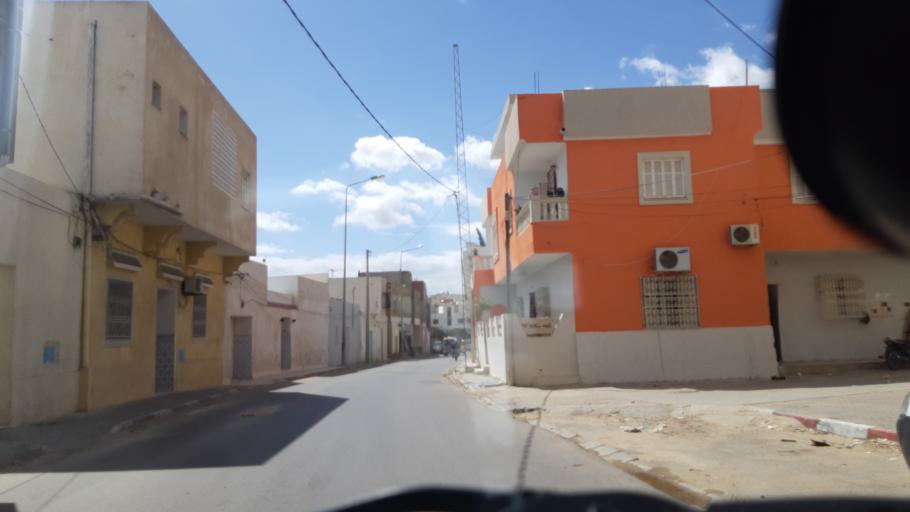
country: TN
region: Susah
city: Akouda
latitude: 35.8779
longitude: 10.5368
